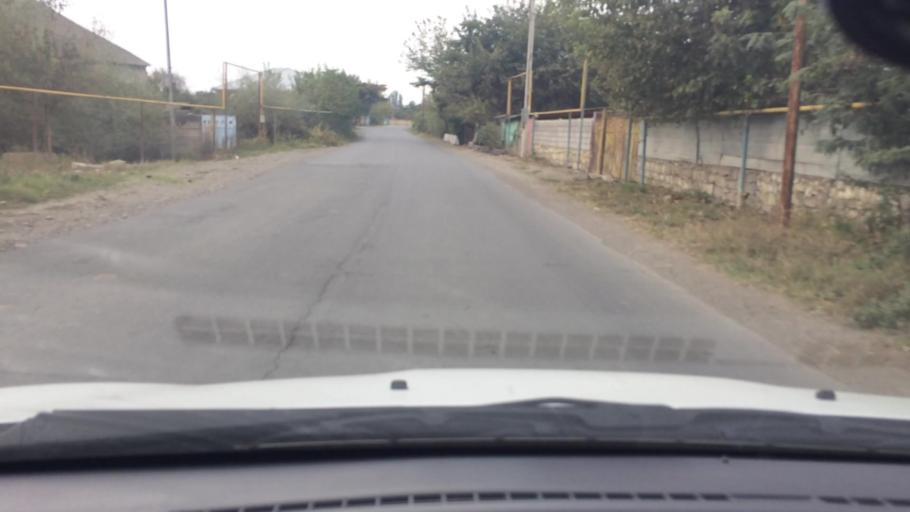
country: GE
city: Naghvarevi
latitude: 41.3507
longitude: 44.8649
